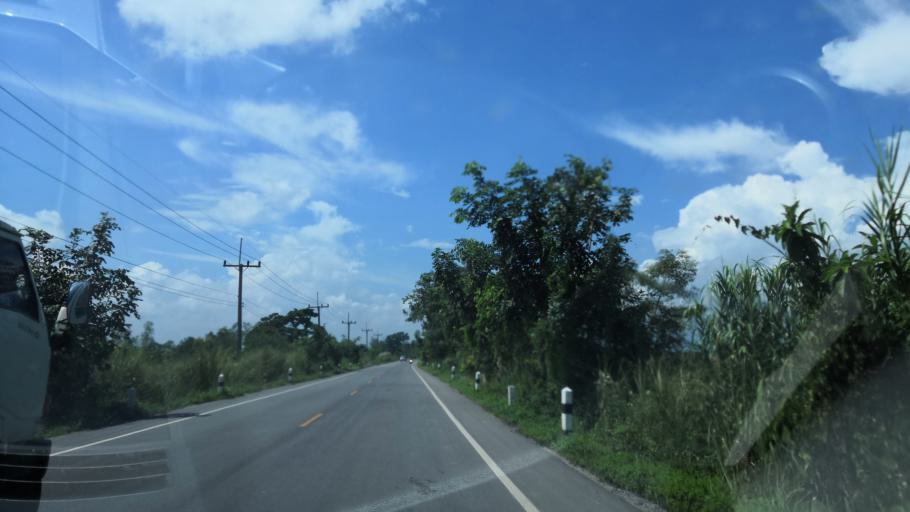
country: TH
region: Chiang Rai
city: Wiang Chiang Rung
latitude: 19.9653
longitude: 99.9959
